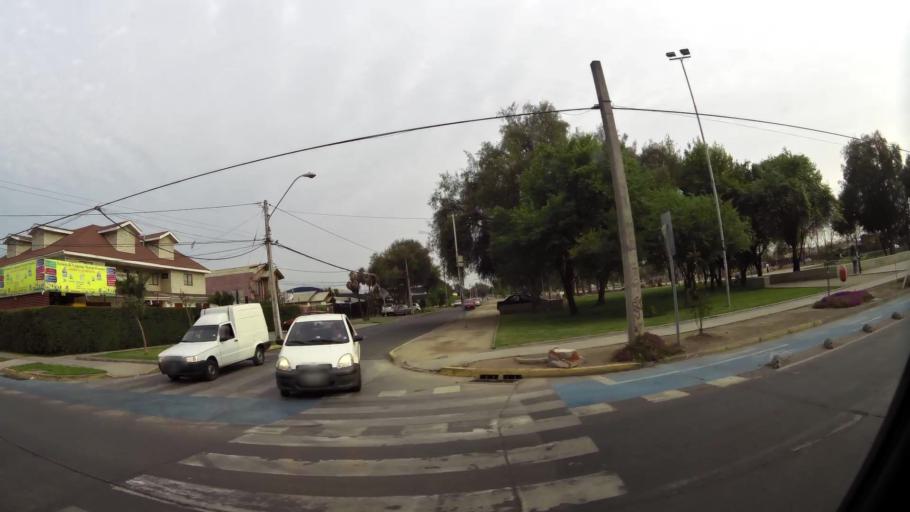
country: CL
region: Santiago Metropolitan
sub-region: Provincia de Santiago
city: Lo Prado
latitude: -33.5216
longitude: -70.7782
